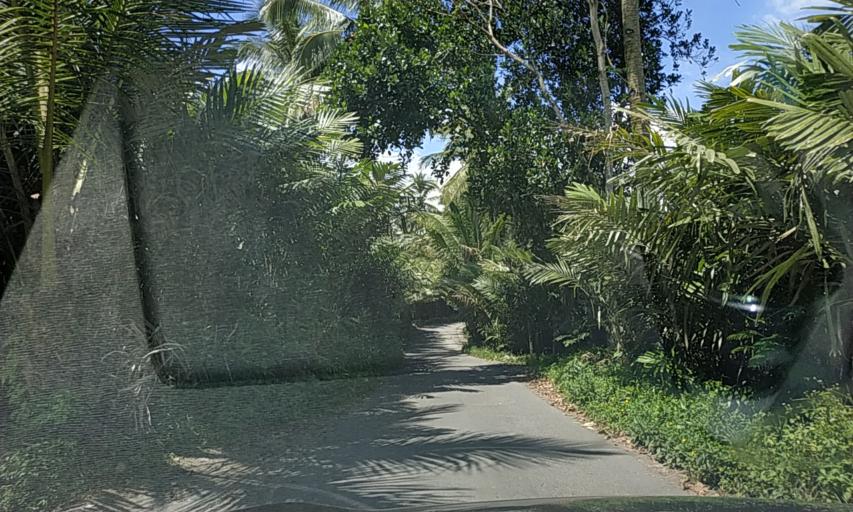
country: ID
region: Central Java
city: Muntilan
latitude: -7.5986
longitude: 110.3537
